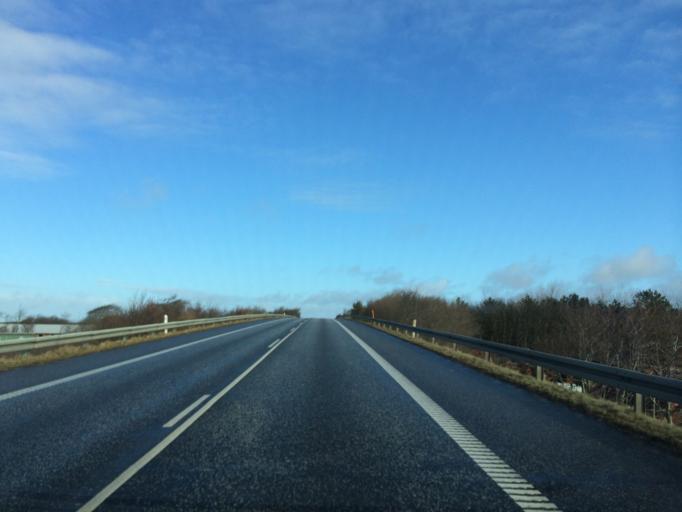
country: DK
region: Central Jutland
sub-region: Holstebro Kommune
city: Ulfborg
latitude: 56.2780
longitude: 8.3257
